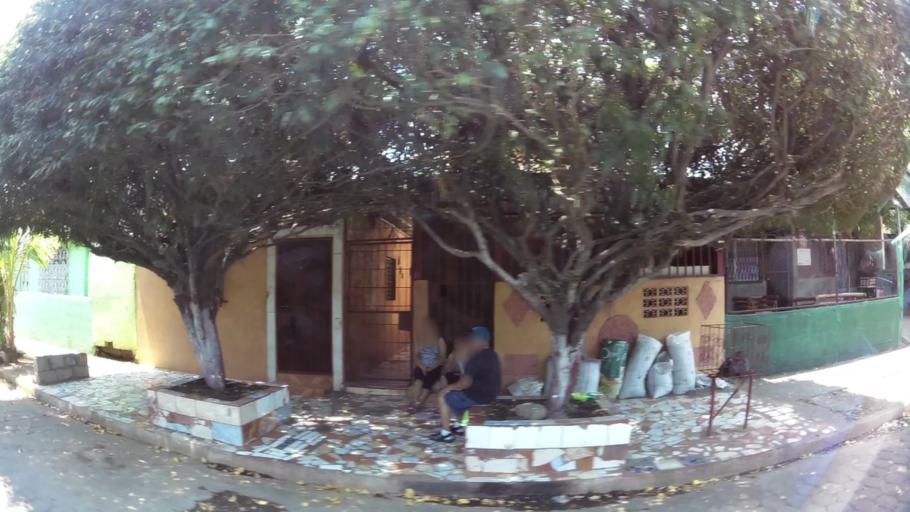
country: NI
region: Managua
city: Ciudad Sandino
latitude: 12.1518
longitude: -86.2989
